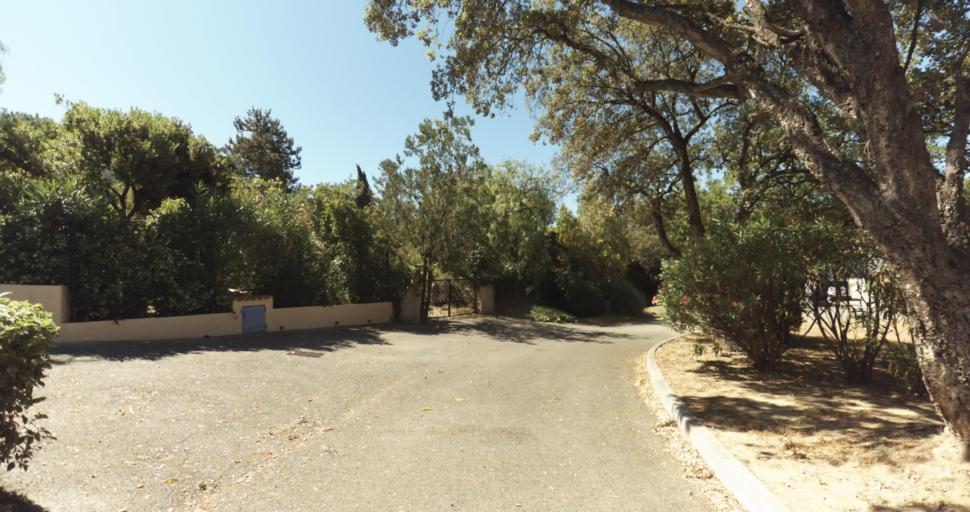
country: FR
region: Provence-Alpes-Cote d'Azur
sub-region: Departement du Var
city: Gassin
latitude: 43.2569
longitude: 6.5994
